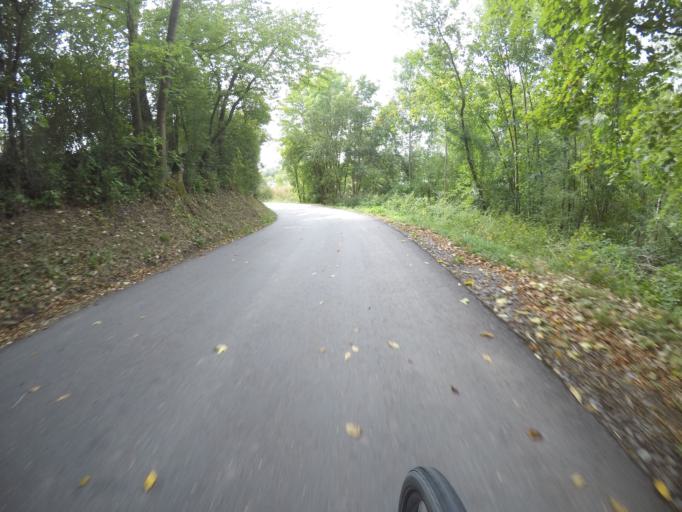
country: DE
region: Baden-Wuerttemberg
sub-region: Karlsruhe Region
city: Oberderdingen
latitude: 49.0907
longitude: 8.7692
